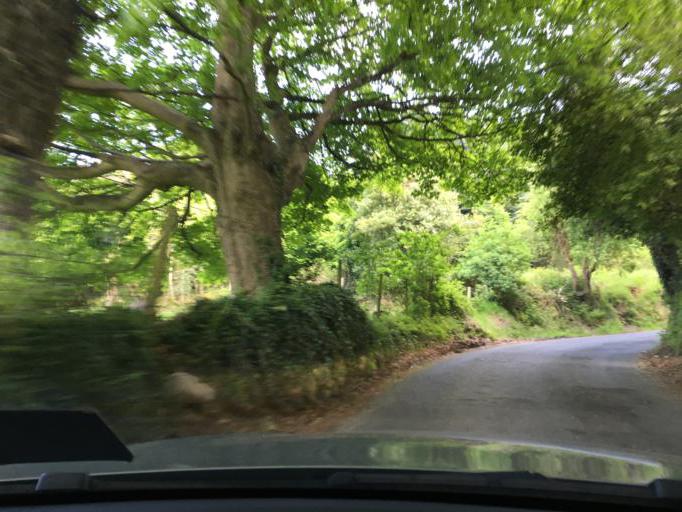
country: IE
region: Leinster
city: Ballinteer
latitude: 53.2590
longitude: -6.2769
